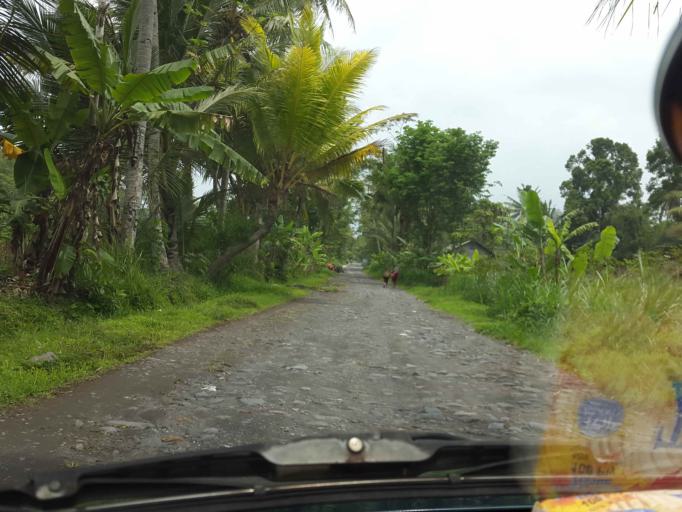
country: ID
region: Central Java
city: Muntilan
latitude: -7.6010
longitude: 110.3058
